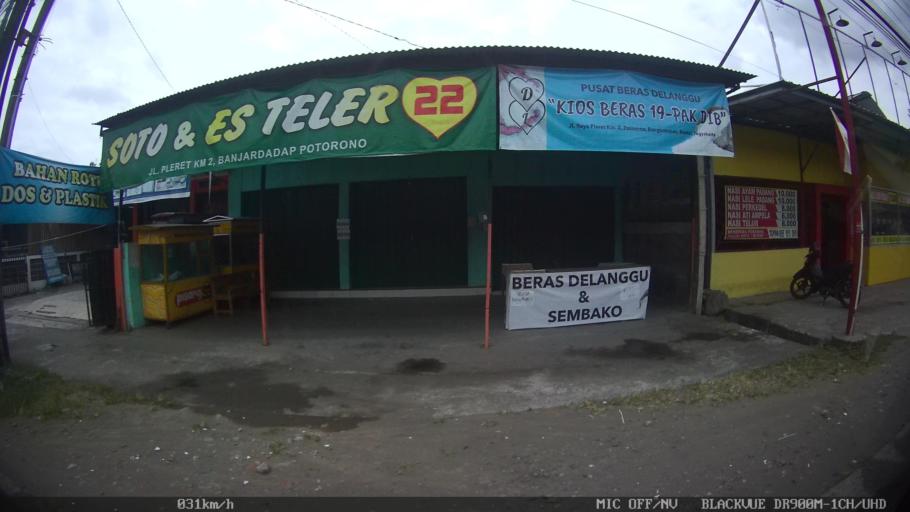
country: ID
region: Daerah Istimewa Yogyakarta
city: Sewon
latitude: -7.8470
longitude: 110.4106
